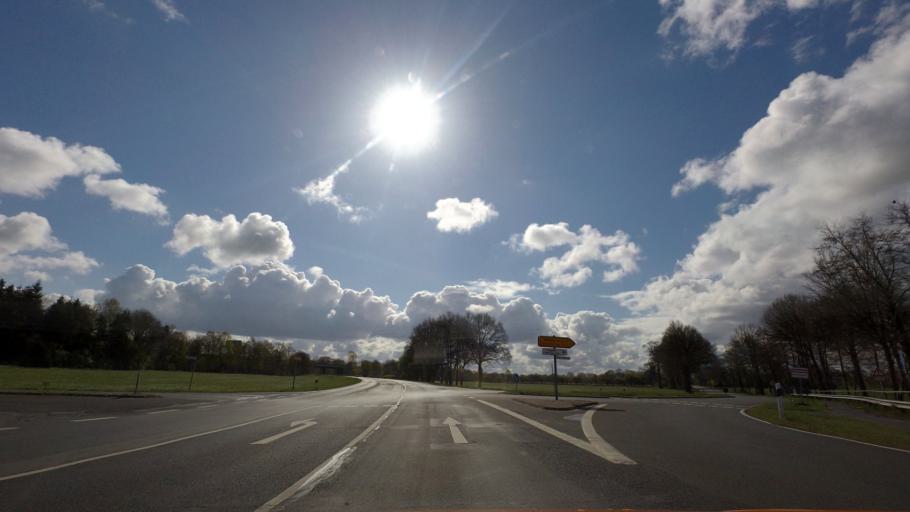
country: DE
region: Lower Saxony
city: Oldenburg
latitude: 53.1036
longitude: 8.2806
